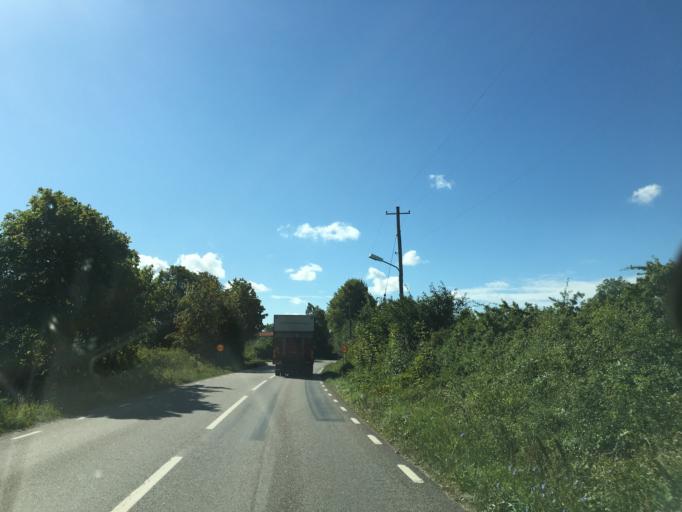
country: SE
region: Kalmar
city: Faerjestaden
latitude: 56.6409
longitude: 16.5164
